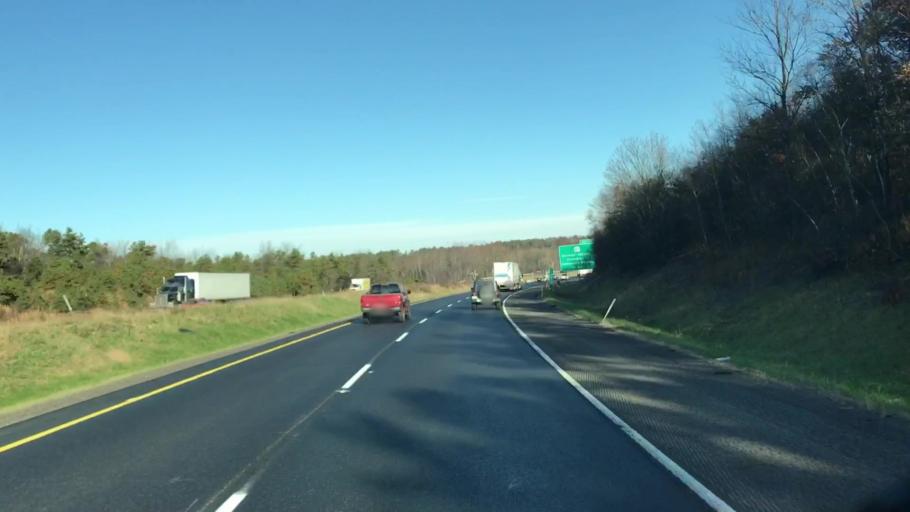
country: US
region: Pennsylvania
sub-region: Schuylkill County
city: McAdoo
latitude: 40.8954
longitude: -76.0286
